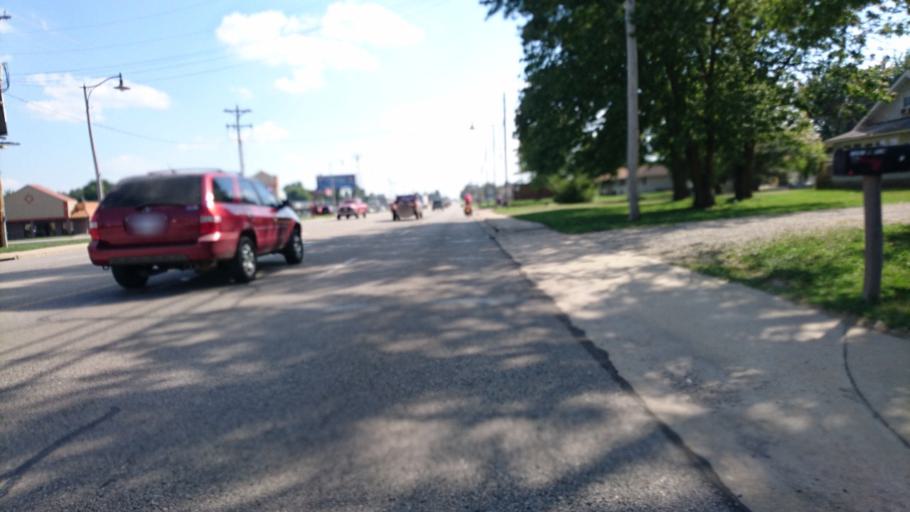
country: US
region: Missouri
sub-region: Laclede County
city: Lebanon
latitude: 37.6617
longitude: -92.6677
